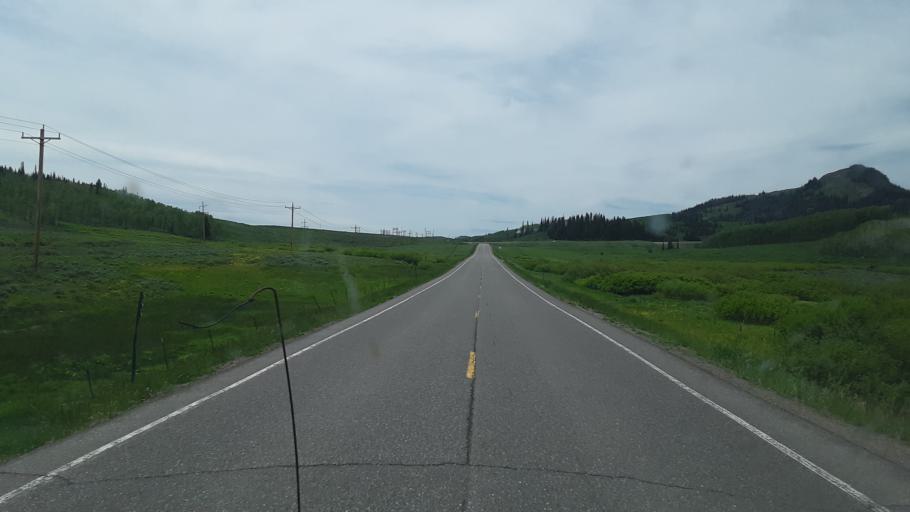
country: US
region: Colorado
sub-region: Routt County
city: Steamboat Springs
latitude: 40.3888
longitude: -106.5716
